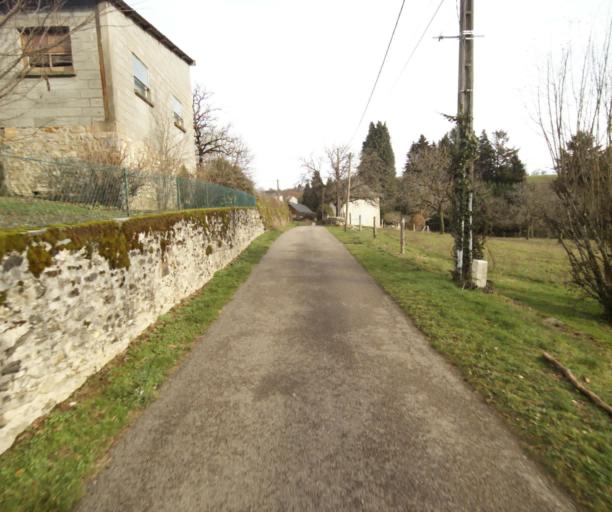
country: FR
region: Limousin
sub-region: Departement de la Correze
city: Saint-Mexant
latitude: 45.2618
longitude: 1.6749
